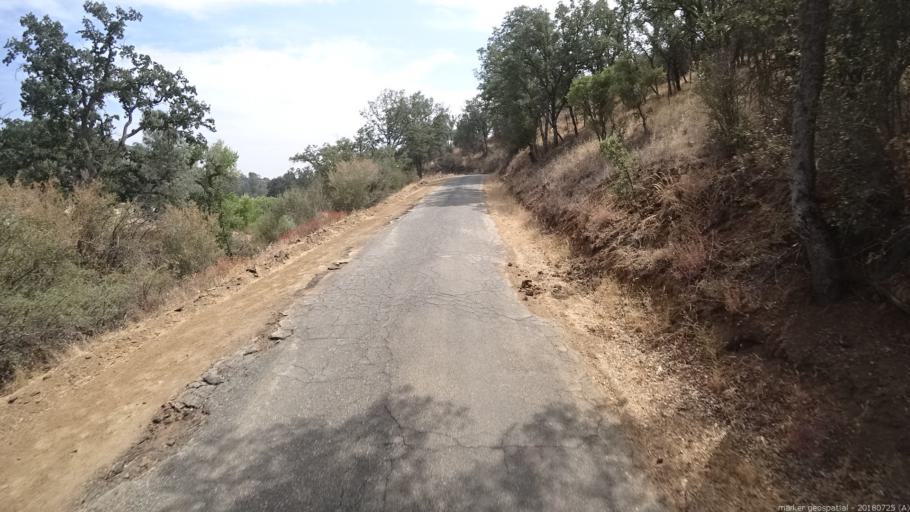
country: US
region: California
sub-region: Fresno County
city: Coalinga
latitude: 36.2223
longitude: -120.7072
